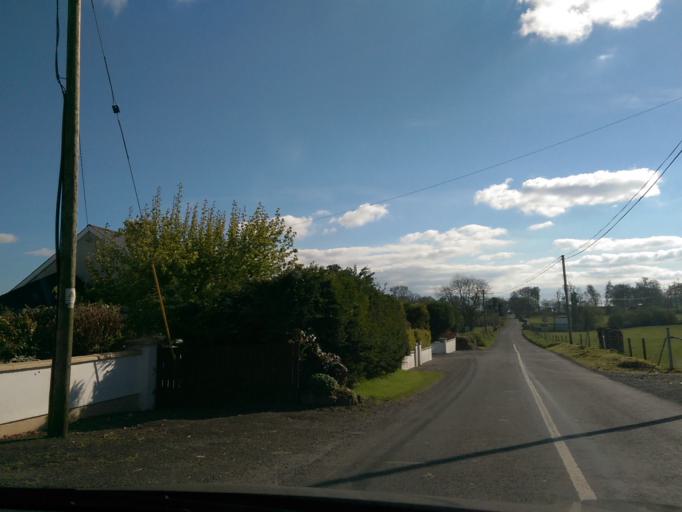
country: IE
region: Leinster
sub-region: Uibh Fhaili
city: Birr
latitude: 53.0790
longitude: -7.9310
